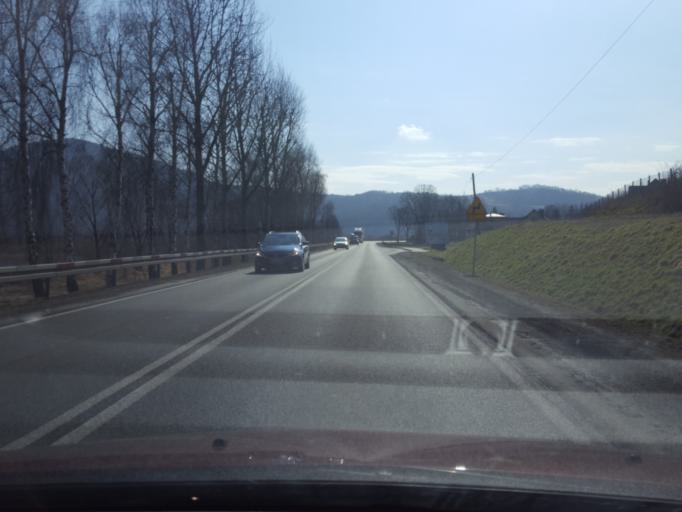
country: PL
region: Lesser Poland Voivodeship
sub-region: Powiat nowosadecki
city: Lososina Dolna
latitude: 49.7015
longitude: 20.6563
